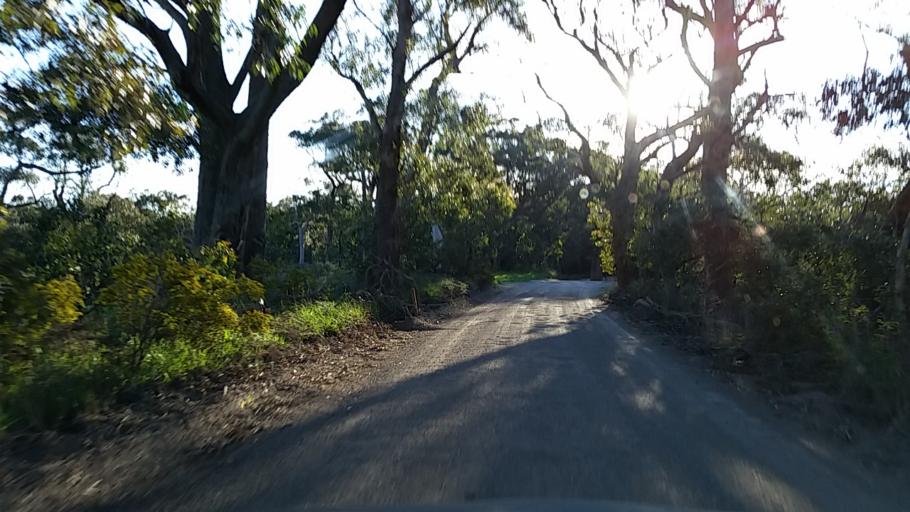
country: AU
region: South Australia
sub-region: Mount Barker
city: Meadows
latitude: -35.2297
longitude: 138.7408
